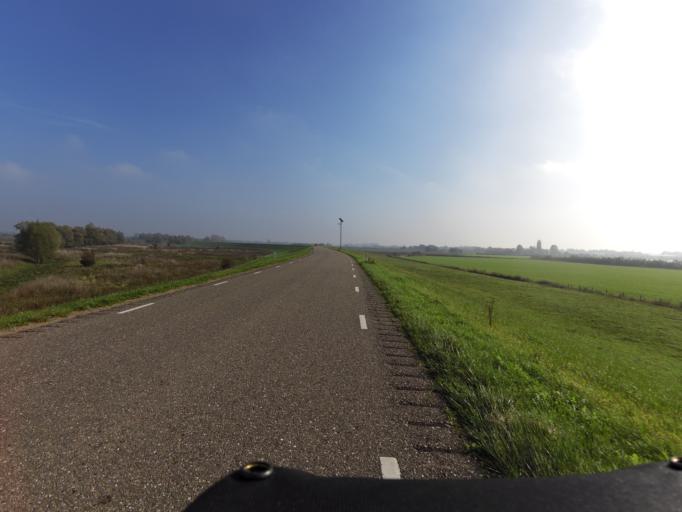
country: NL
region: Gelderland
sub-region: Gemeente Groesbeek
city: Berg en Dal
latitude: 51.8492
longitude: 5.9732
